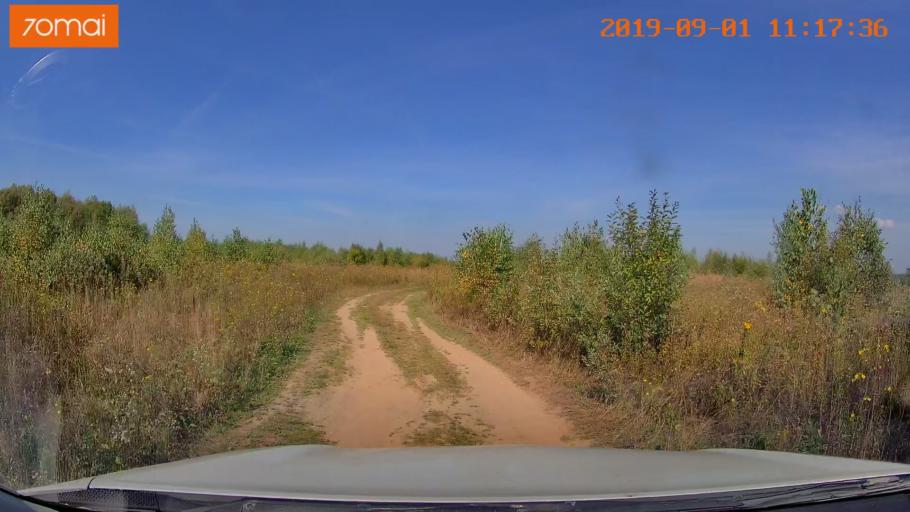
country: RU
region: Kaluga
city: Detchino
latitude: 54.8250
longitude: 36.3667
